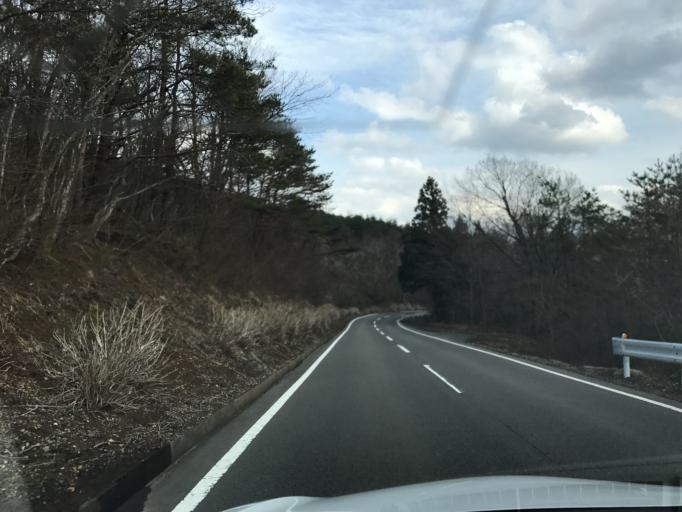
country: JP
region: Miyagi
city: Shiroishi
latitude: 38.0267
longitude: 140.5419
